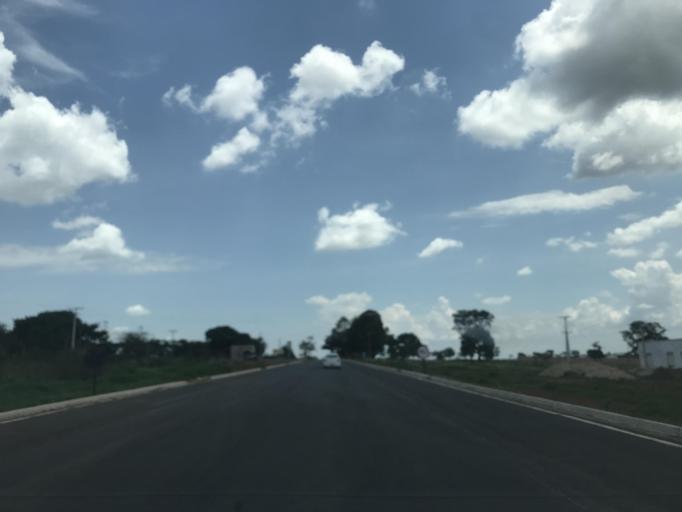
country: BR
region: Goias
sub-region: Bela Vista De Goias
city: Bela Vista de Goias
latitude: -17.0686
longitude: -48.6575
